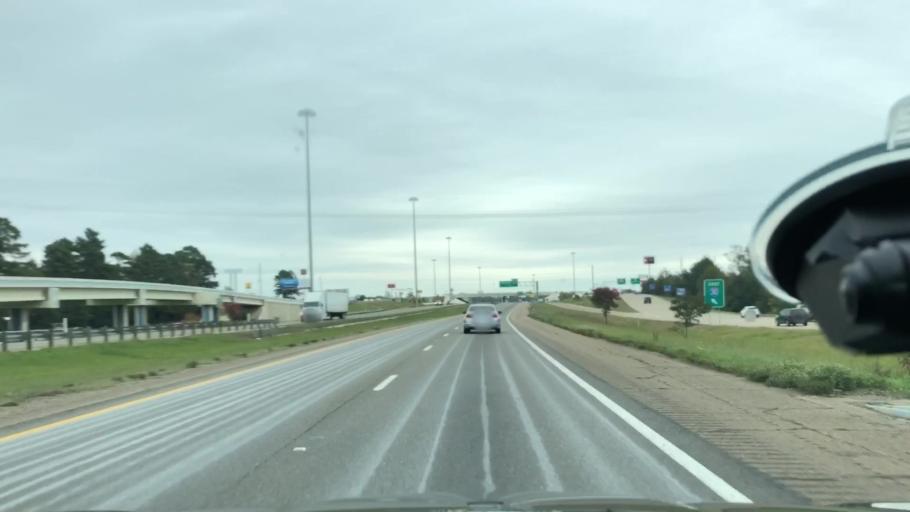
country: US
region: Arkansas
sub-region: Miller County
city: Texarkana
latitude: 33.4701
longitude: -94.0500
